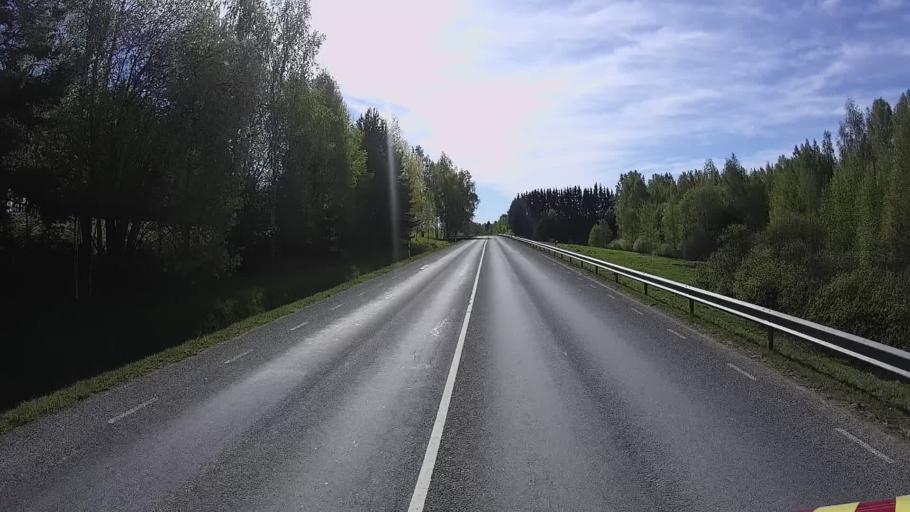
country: EE
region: Polvamaa
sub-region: Polva linn
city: Polva
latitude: 58.1610
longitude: 27.1602
